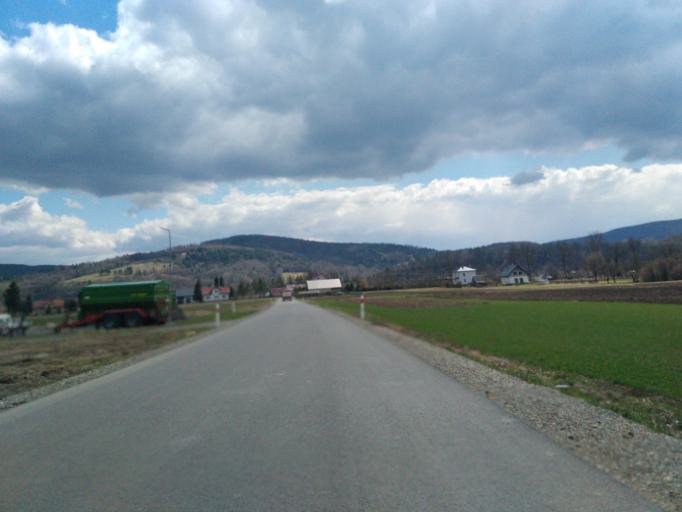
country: PL
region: Subcarpathian Voivodeship
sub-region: Powiat sanocki
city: Sanok
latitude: 49.6270
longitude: 22.2709
